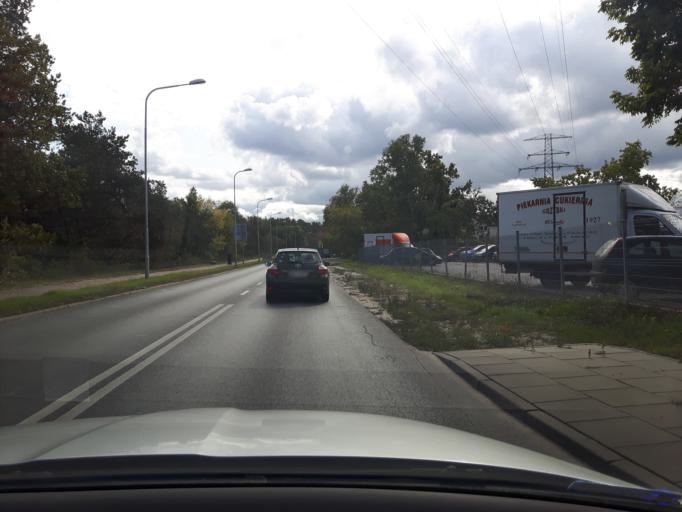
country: PL
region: Masovian Voivodeship
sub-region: Warszawa
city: Rembertow
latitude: 52.2365
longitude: 21.1426
